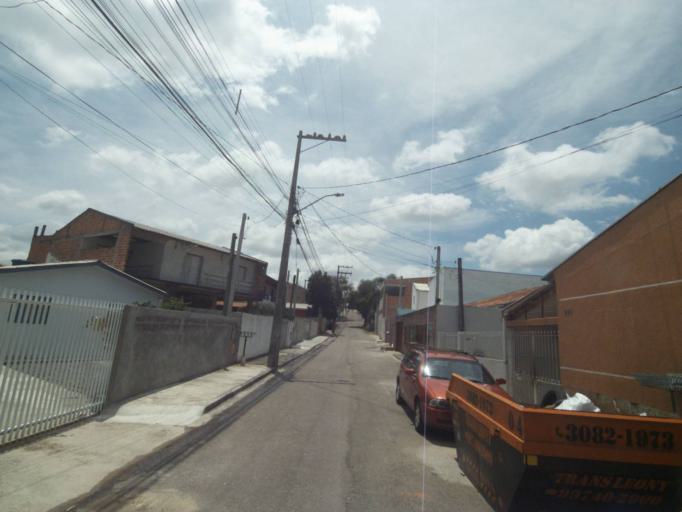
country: BR
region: Parana
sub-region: Curitiba
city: Curitiba
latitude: -25.4597
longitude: -49.3478
